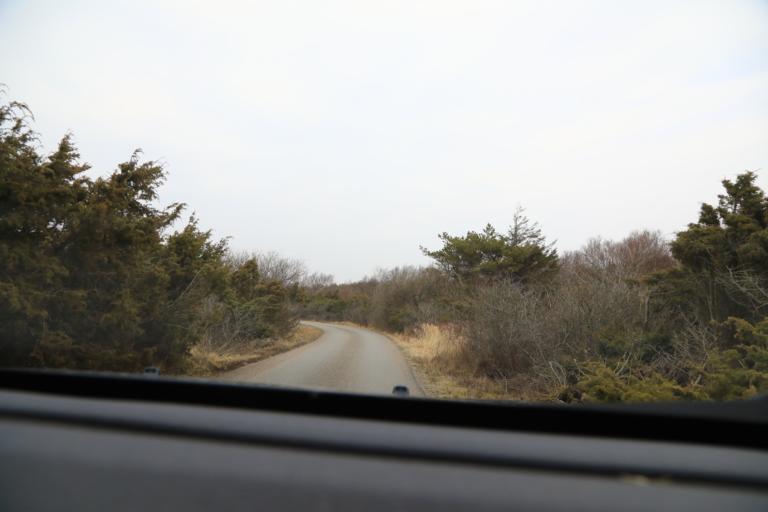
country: SE
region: Halland
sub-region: Kungsbacka Kommun
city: Frillesas
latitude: 57.2668
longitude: 12.1093
